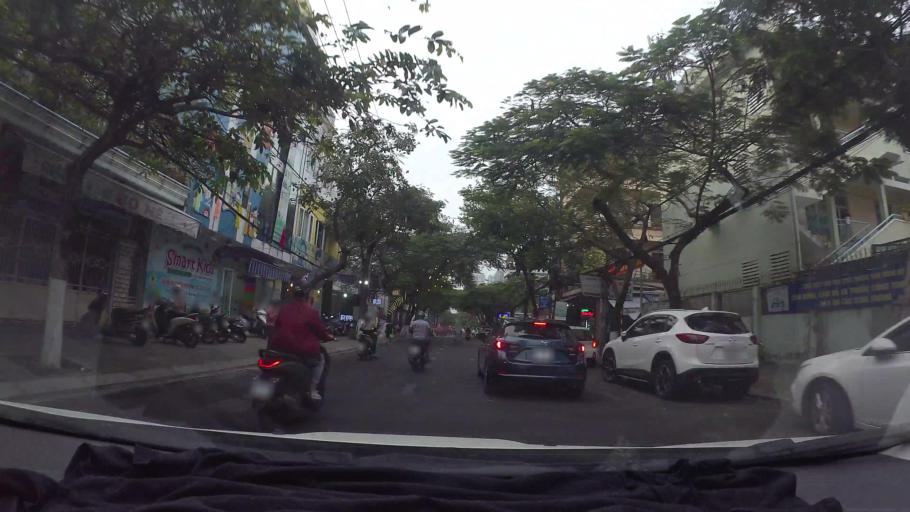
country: VN
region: Da Nang
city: Da Nang
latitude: 16.0738
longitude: 108.2207
